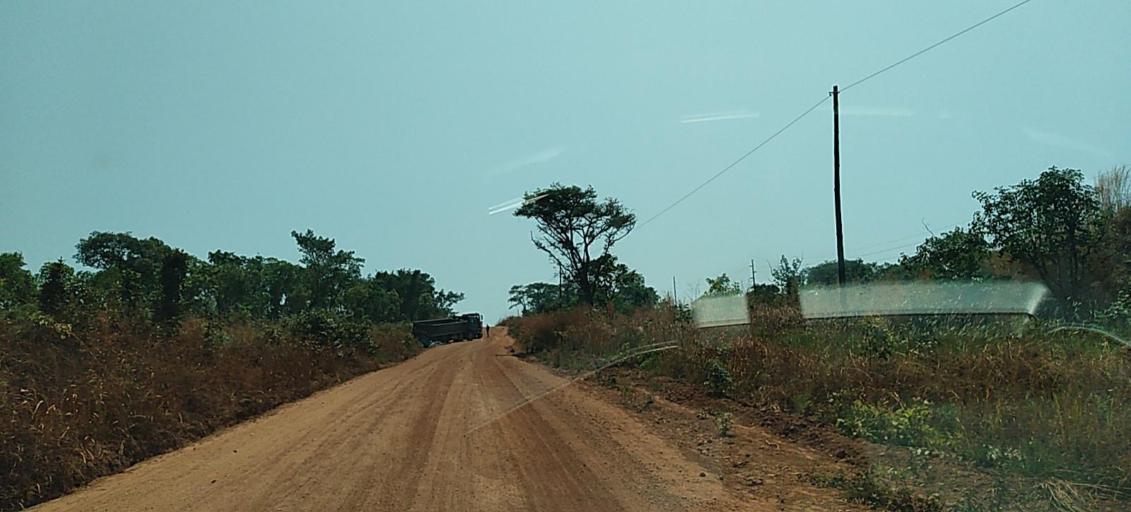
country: ZM
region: North-Western
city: Kansanshi
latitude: -12.0066
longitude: 26.5798
